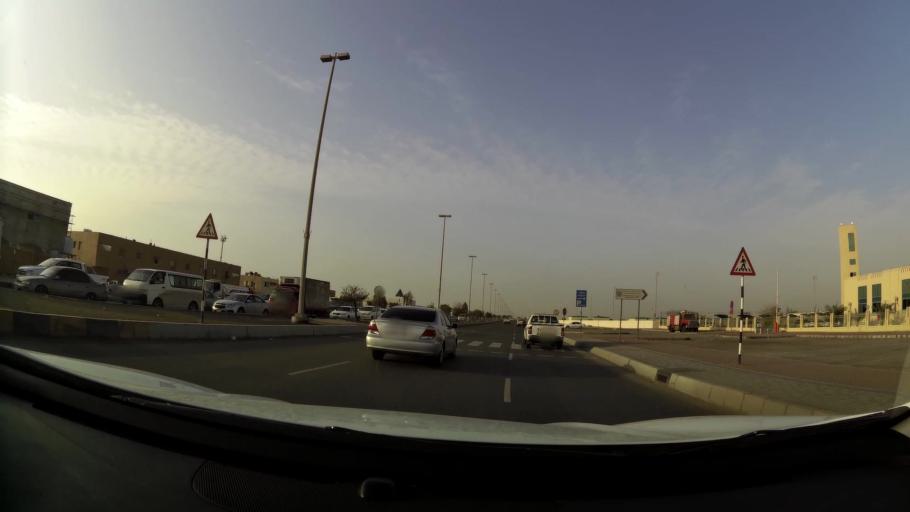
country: AE
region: Abu Dhabi
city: Abu Dhabi
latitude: 24.3464
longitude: 54.5024
